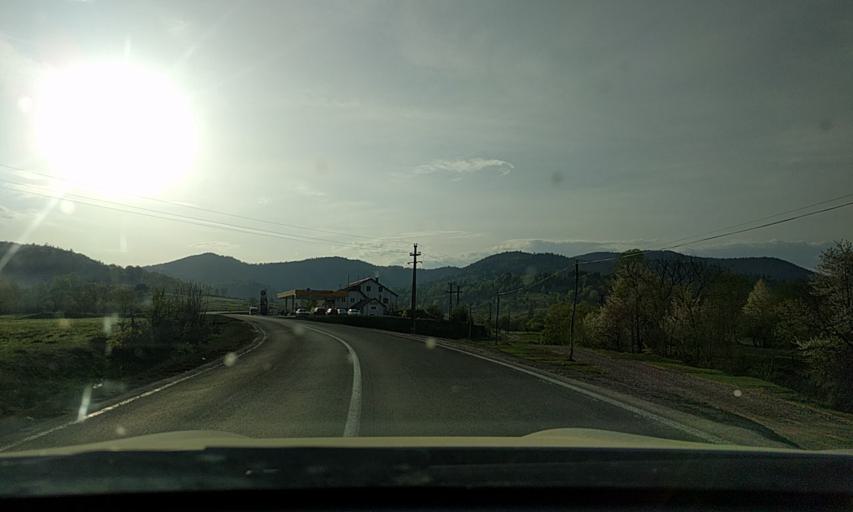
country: RO
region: Covasna
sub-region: Comuna Bretcu
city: Bretcu
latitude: 46.0455
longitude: 26.3243
